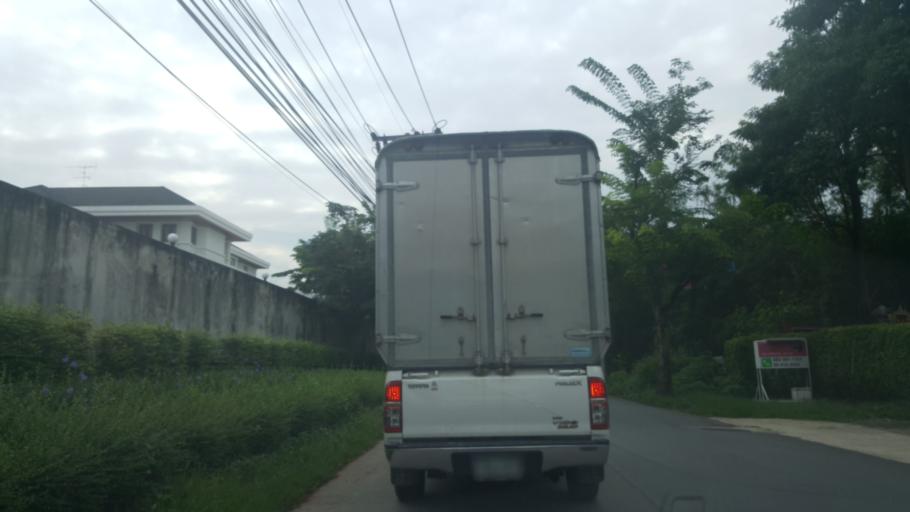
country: TH
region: Bangkok
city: Bang Bon
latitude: 13.6757
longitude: 100.3997
